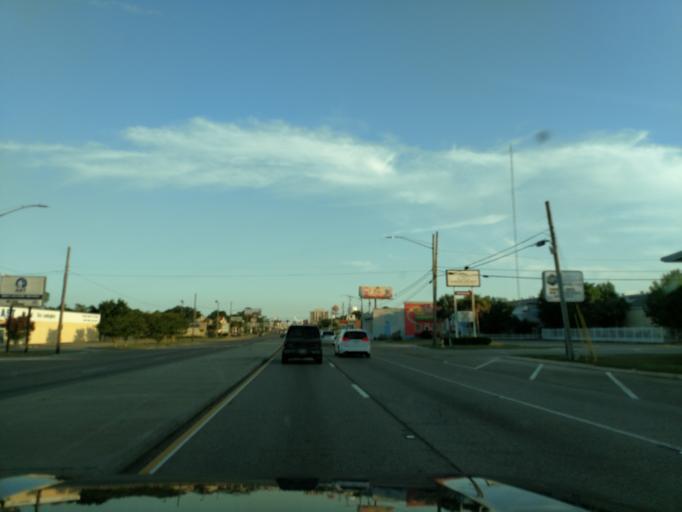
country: US
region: Mississippi
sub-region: Harrison County
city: Gulfport
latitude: 30.3831
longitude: -89.0932
